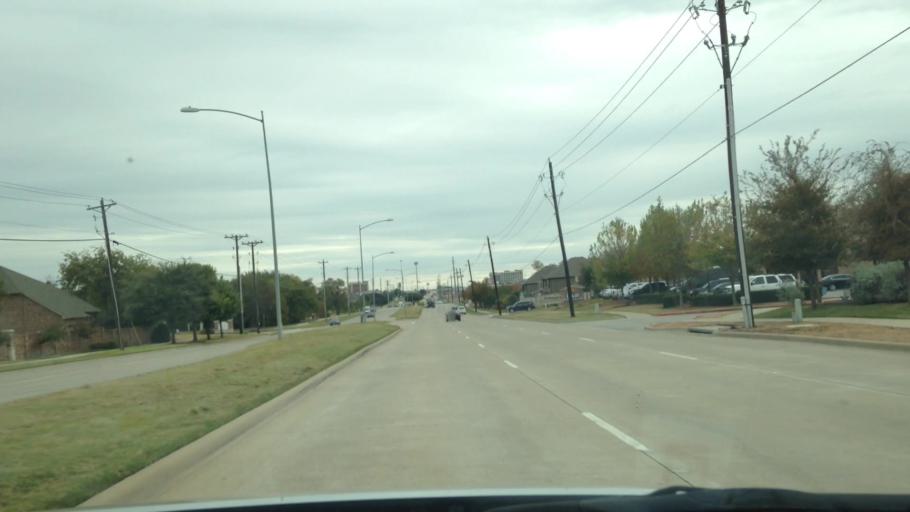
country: US
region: Texas
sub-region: Collin County
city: Allen
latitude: 33.1298
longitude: -96.6738
